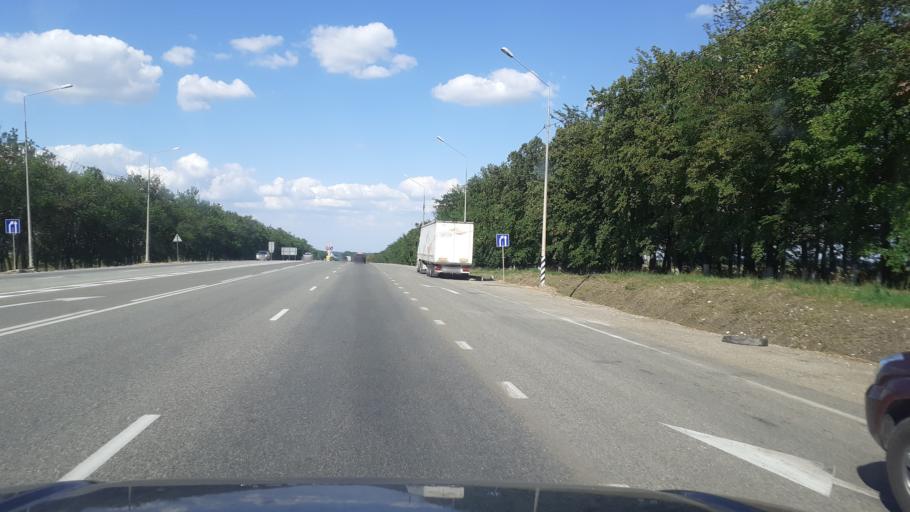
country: RU
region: Krasnodarskiy
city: Severskaya
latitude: 44.8400
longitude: 38.6952
